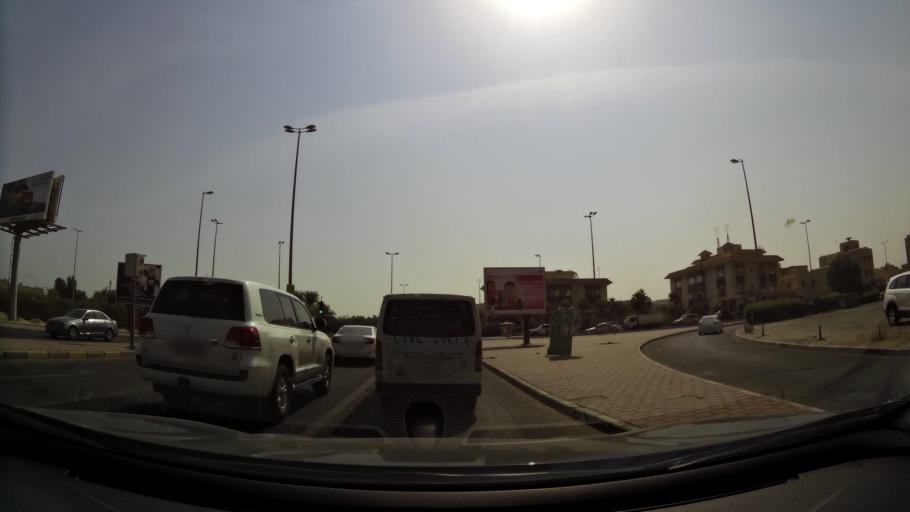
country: KW
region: Al Ahmadi
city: Al Manqaf
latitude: 29.0926
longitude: 48.1375
